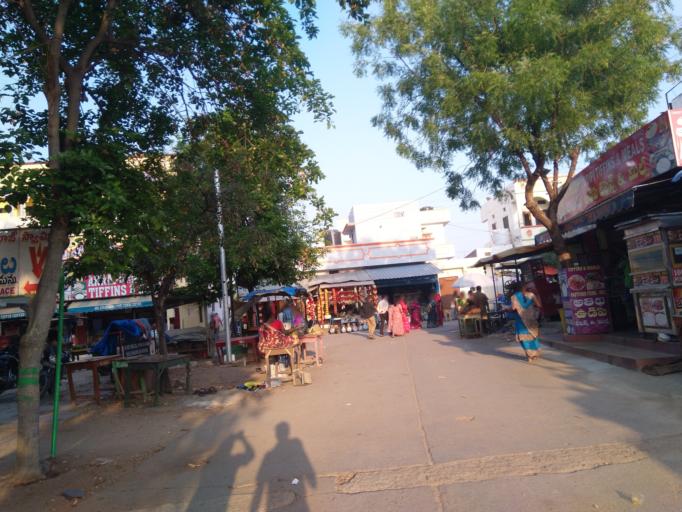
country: IN
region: Telangana
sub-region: Rangareddi
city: Sriramnagar
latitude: 17.3580
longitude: 78.2993
